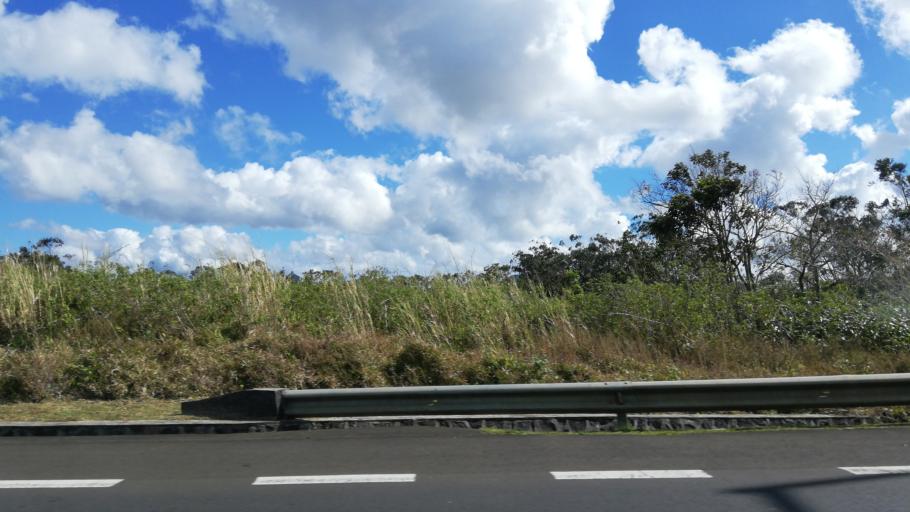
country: MU
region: Moka
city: La Dagotiere
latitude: -20.2525
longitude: 57.5662
